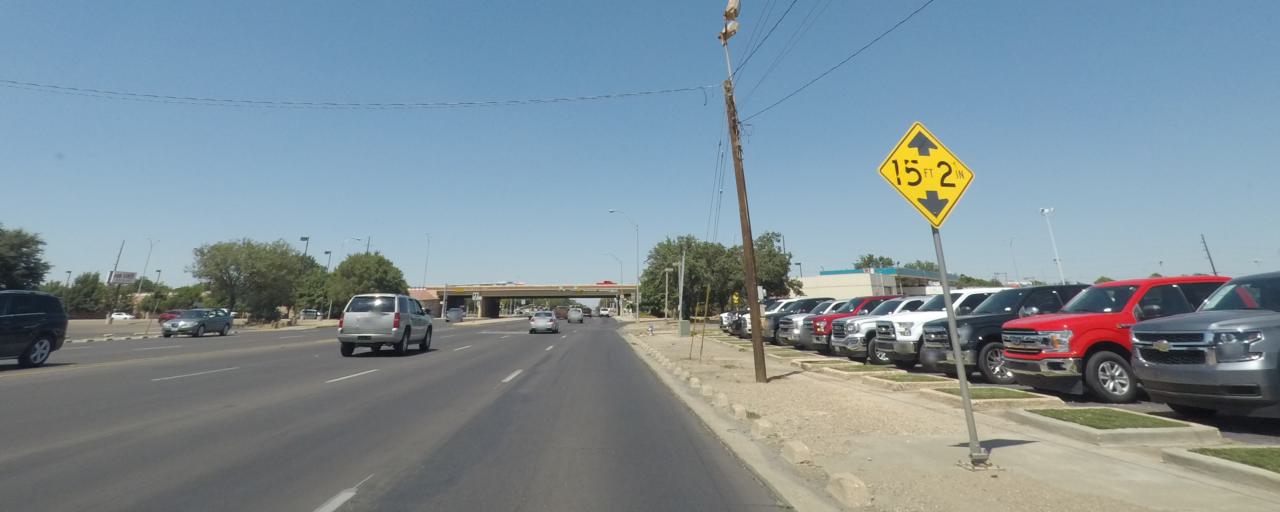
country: US
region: Texas
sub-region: Lubbock County
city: Lubbock
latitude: 33.5276
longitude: -101.8876
